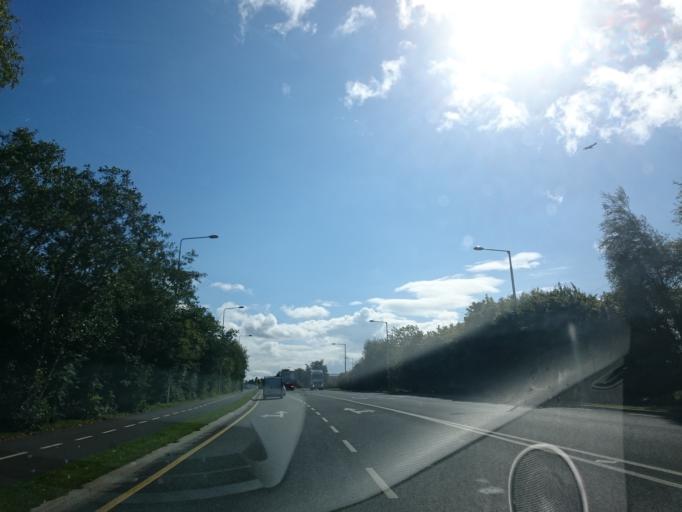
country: IE
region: Leinster
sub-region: Kilkenny
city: Kilkenny
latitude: 52.6363
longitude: -7.2532
